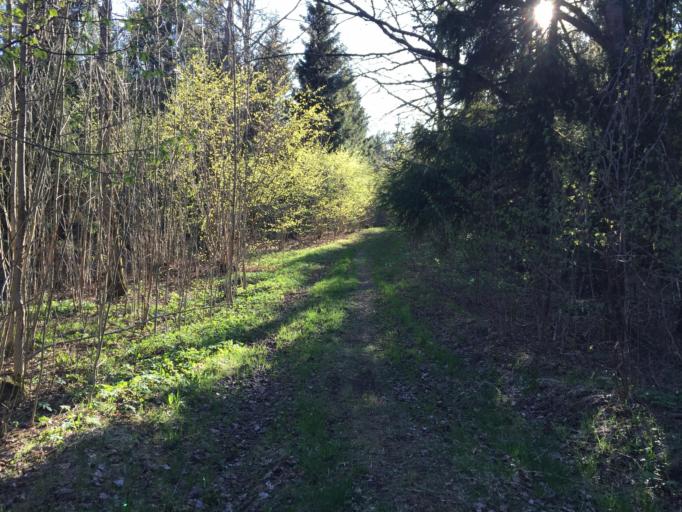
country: LV
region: Vecpiebalga
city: Vecpiebalga
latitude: 56.8666
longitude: 25.9496
